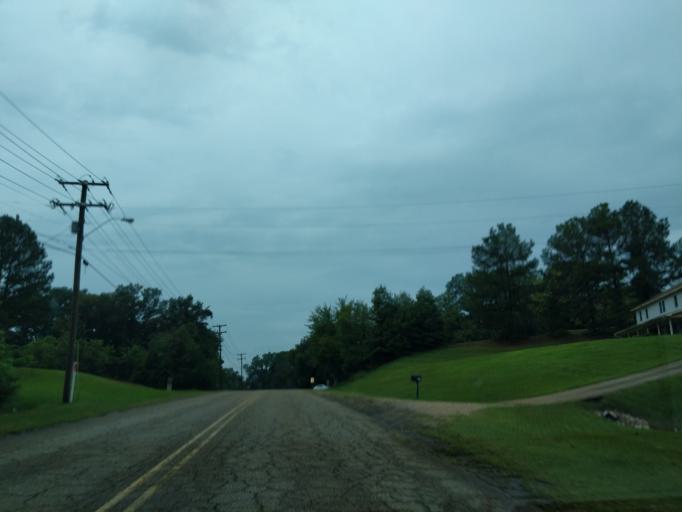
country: US
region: Mississippi
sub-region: Warren County
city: Vicksburg
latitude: 32.3172
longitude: -90.8875
